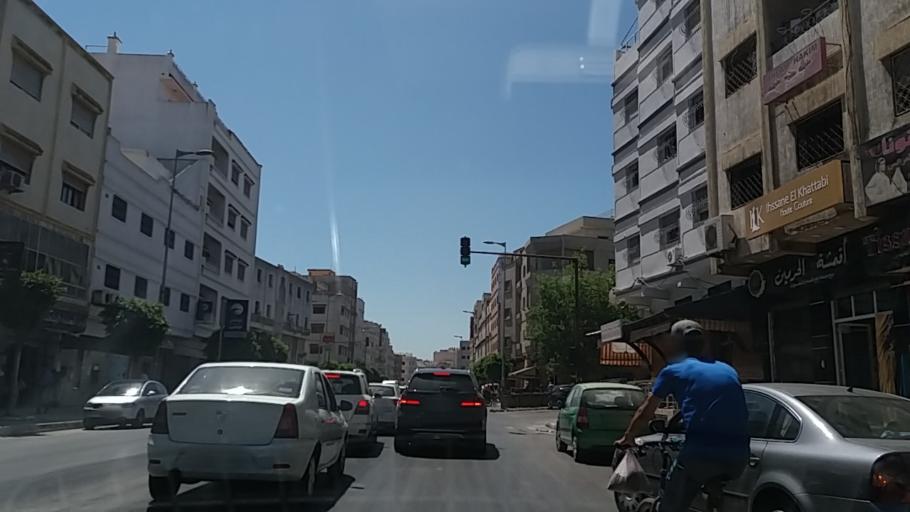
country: MA
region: Tanger-Tetouan
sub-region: Tanger-Assilah
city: Tangier
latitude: 35.7605
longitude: -5.8024
